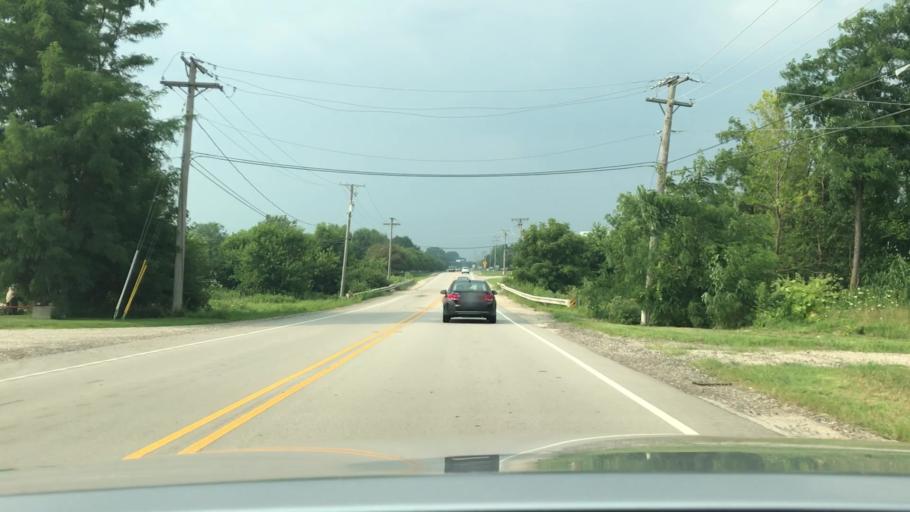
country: US
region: Illinois
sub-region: Will County
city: Plainfield
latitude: 41.6293
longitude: -88.2222
